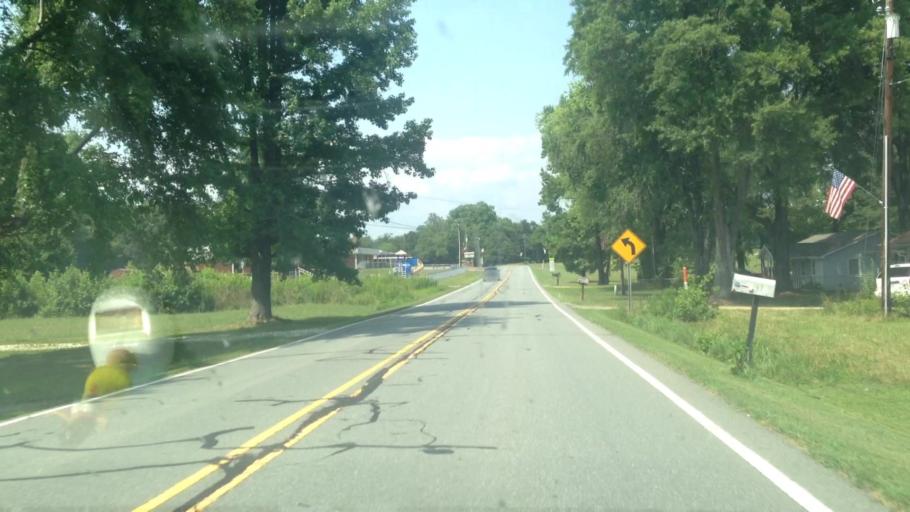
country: US
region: North Carolina
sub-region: Stokes County
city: Walnut Cove
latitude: 36.3270
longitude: -80.0485
